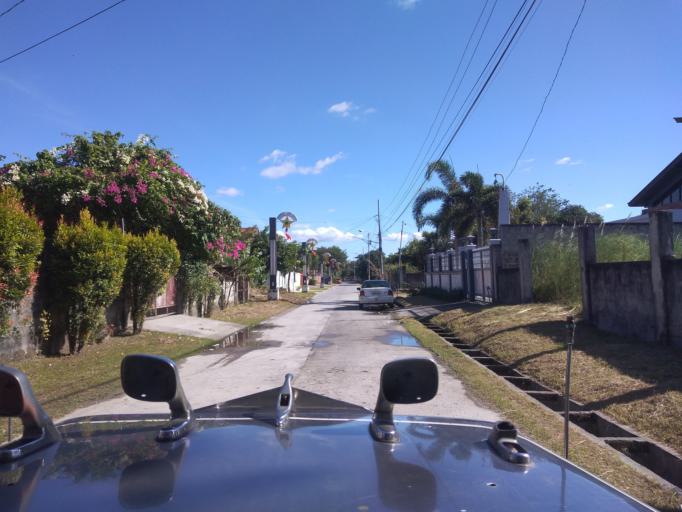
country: PH
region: Central Luzon
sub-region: Province of Pampanga
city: Bacolor
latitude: 14.9989
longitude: 120.6493
